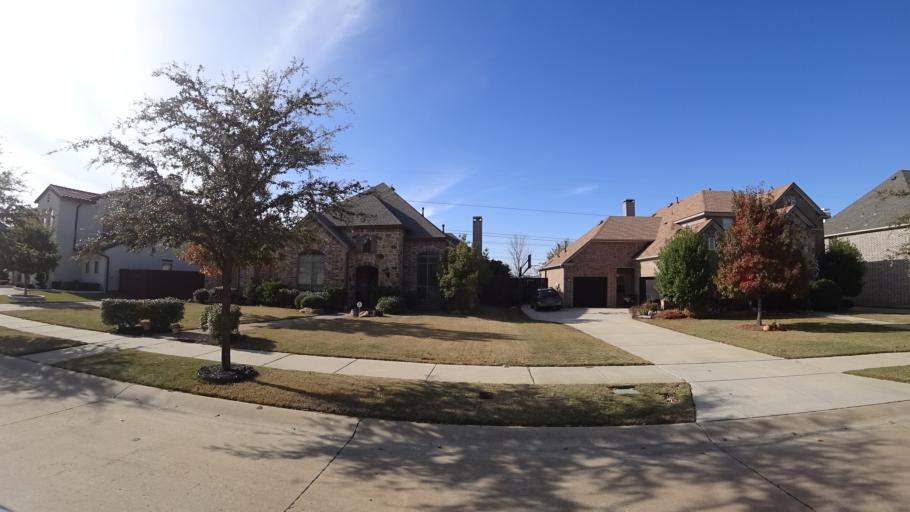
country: US
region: Texas
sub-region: Denton County
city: The Colony
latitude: 33.0285
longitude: -96.9132
